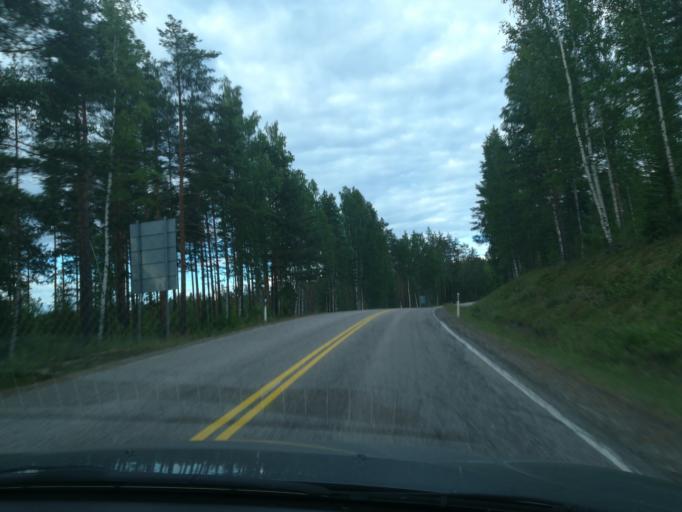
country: FI
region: South Karelia
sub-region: Lappeenranta
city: Savitaipale
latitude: 61.5005
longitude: 27.8351
